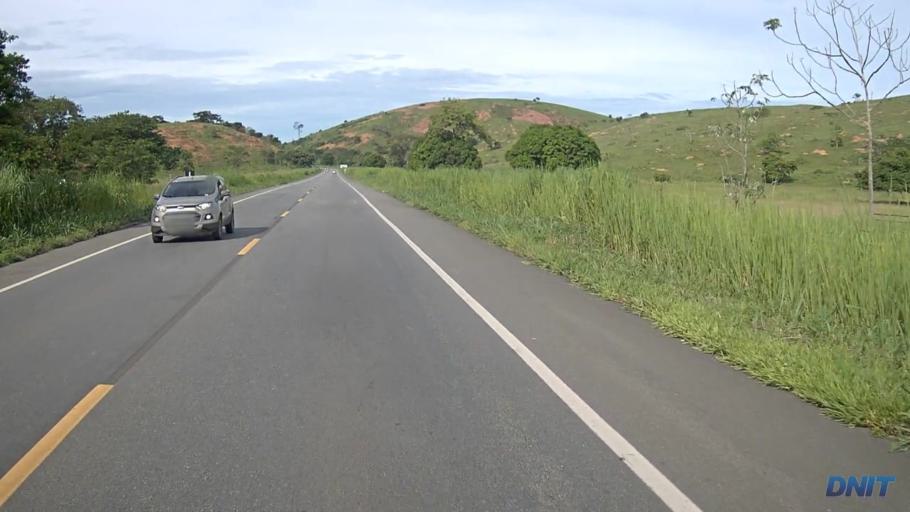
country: BR
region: Minas Gerais
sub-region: Belo Oriente
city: Belo Oriente
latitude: -19.2050
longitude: -42.2955
